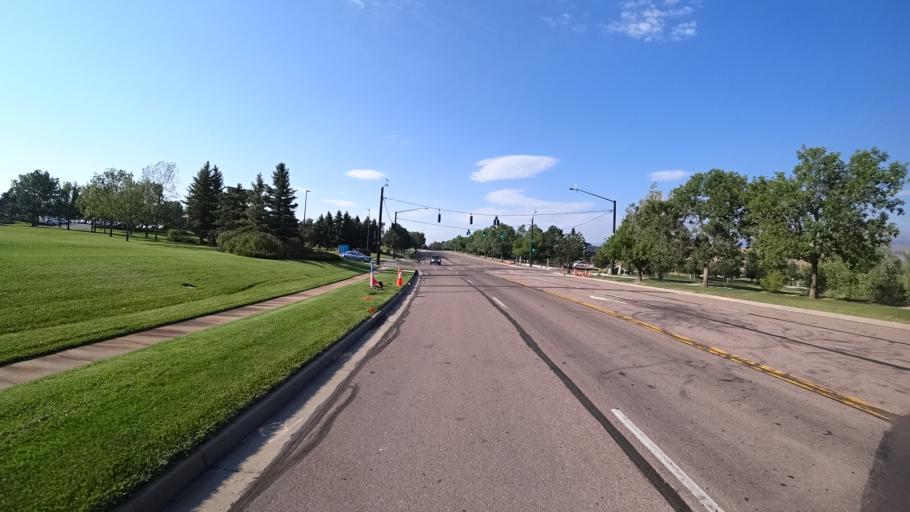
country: US
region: Colorado
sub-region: El Paso County
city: Air Force Academy
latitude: 38.9629
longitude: -104.7917
